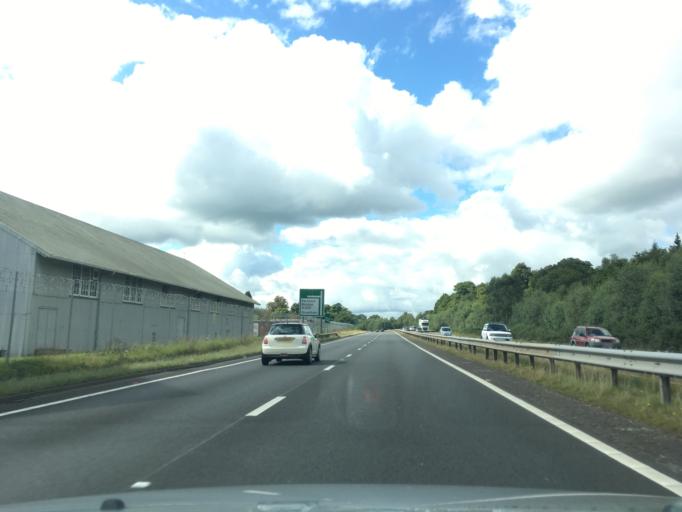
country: GB
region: England
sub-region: Hampshire
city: Bordon
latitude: 51.0749
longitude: -0.8646
